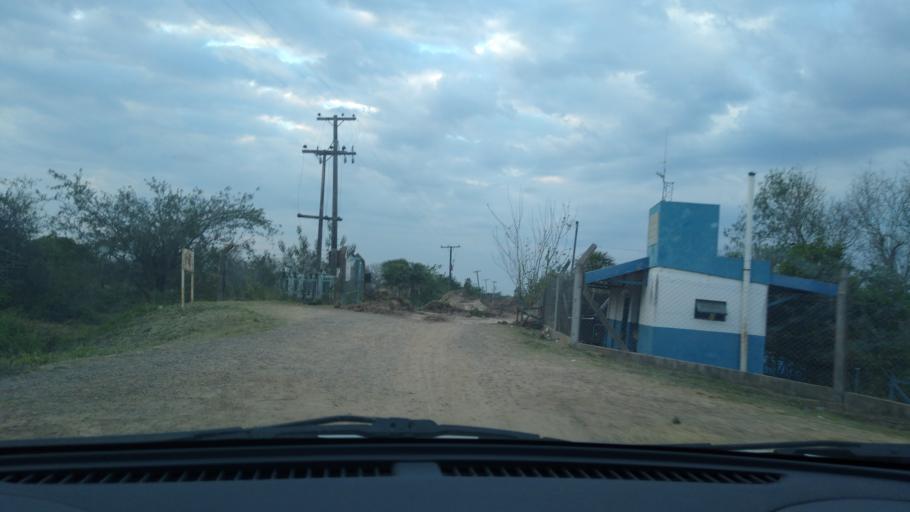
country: AR
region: Chaco
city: Barranqueras
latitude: -27.4683
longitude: -58.9385
